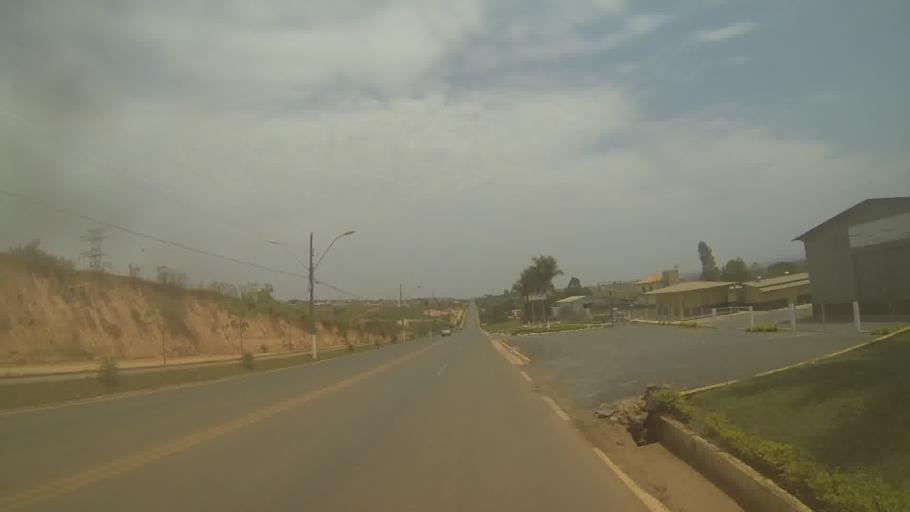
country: BR
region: Minas Gerais
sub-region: Bambui
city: Bambui
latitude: -20.0143
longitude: -45.9533
